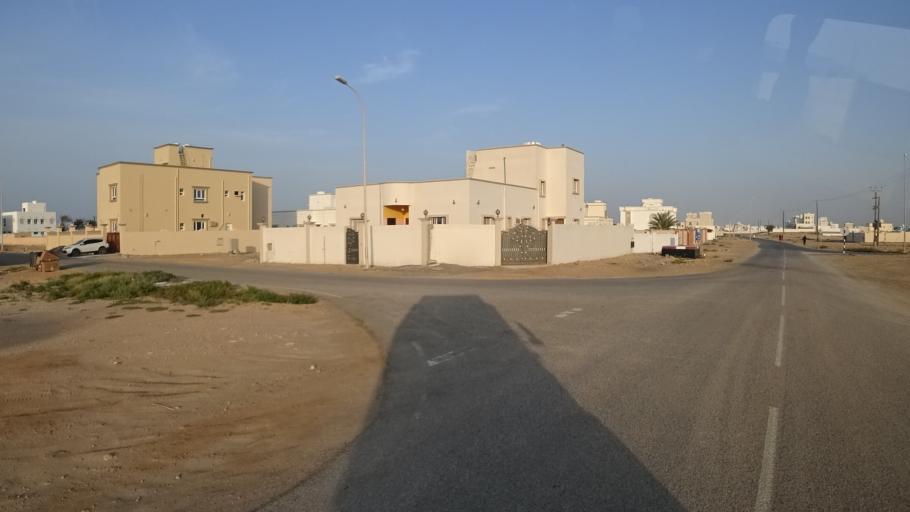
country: OM
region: Ash Sharqiyah
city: Sur
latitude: 22.6206
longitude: 59.4561
